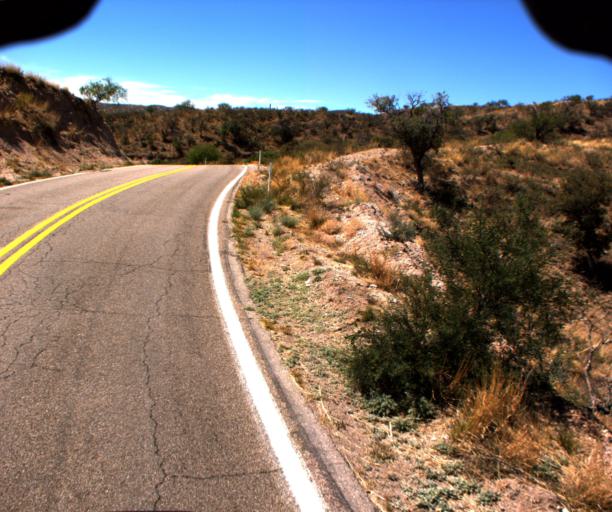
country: US
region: Arizona
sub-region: Santa Cruz County
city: Rio Rico
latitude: 31.3893
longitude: -111.0719
